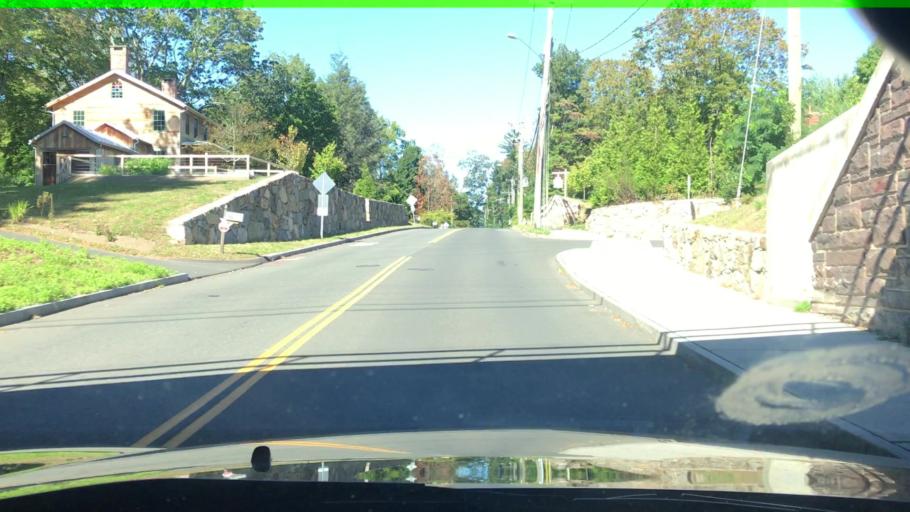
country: US
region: Connecticut
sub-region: Fairfield County
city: Darien
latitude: 41.0775
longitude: -73.4453
